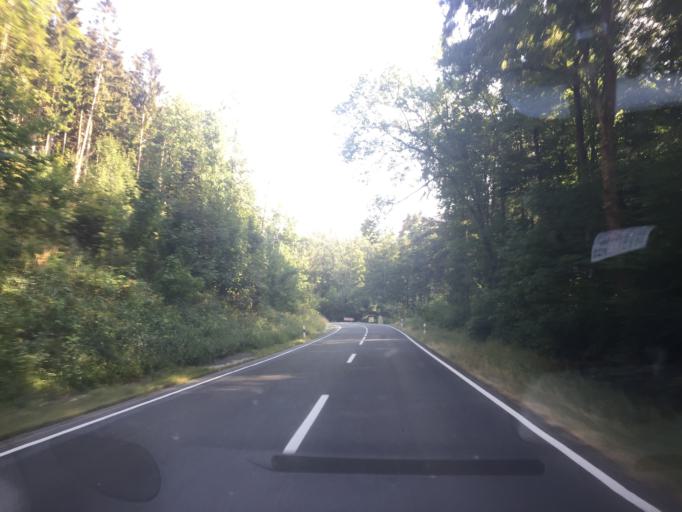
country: DE
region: Saxony-Anhalt
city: Darlingerode
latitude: 51.8028
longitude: 10.7324
